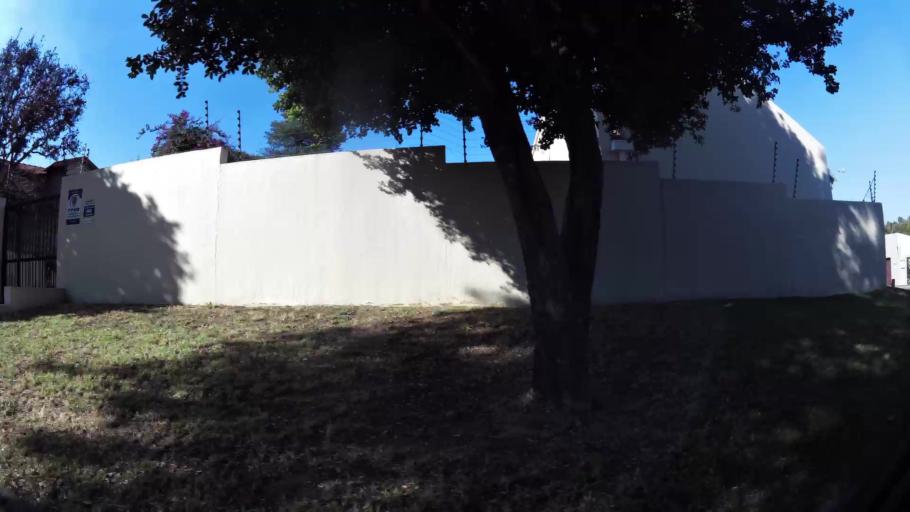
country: ZA
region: Gauteng
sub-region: City of Johannesburg Metropolitan Municipality
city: Roodepoort
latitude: -26.1017
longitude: 27.9534
